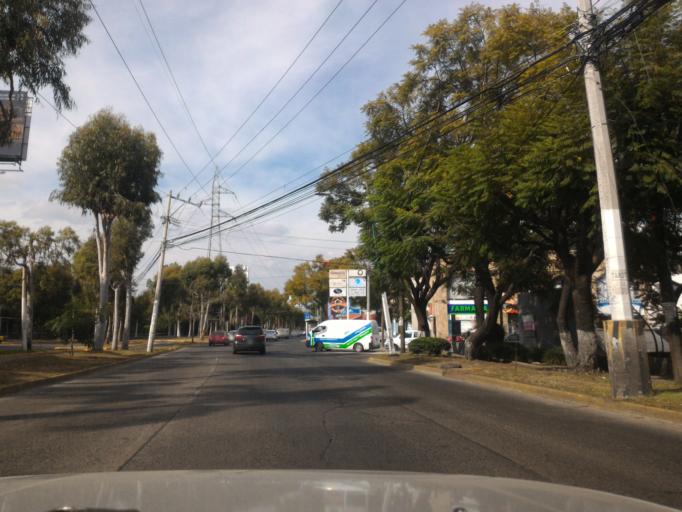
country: MX
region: Jalisco
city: Zapopan2
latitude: 20.6957
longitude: -103.4153
